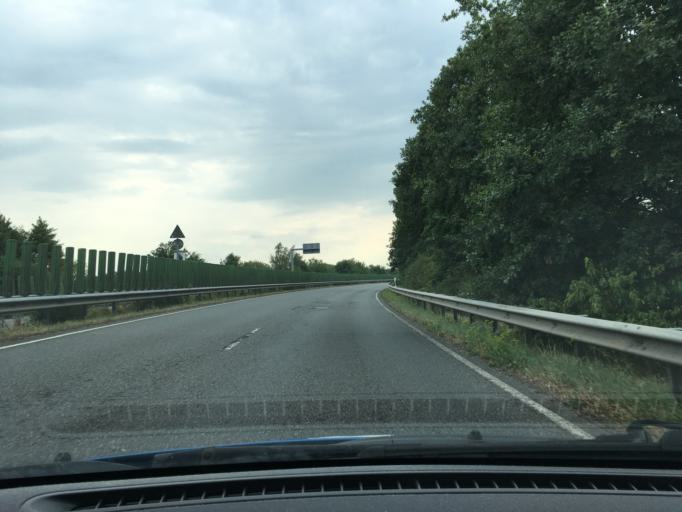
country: DE
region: Lower Saxony
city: Adelheidsdorf
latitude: 52.5227
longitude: 10.0314
